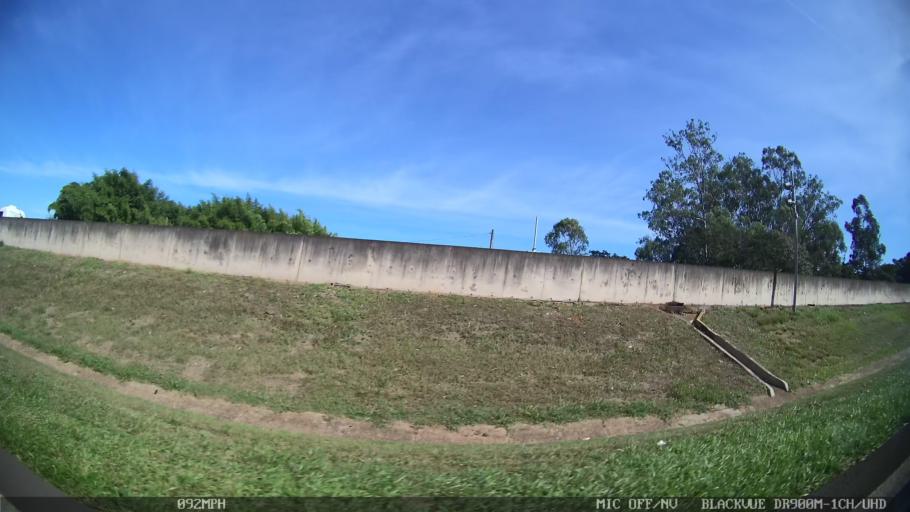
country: BR
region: Sao Paulo
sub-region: Pirassununga
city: Pirassununga
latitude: -21.9932
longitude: -47.4474
